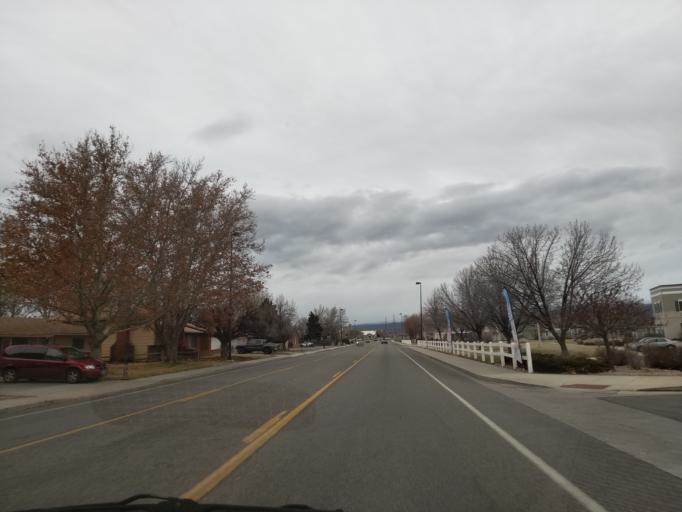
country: US
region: Colorado
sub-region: Mesa County
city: Grand Junction
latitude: 39.0950
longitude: -108.5431
